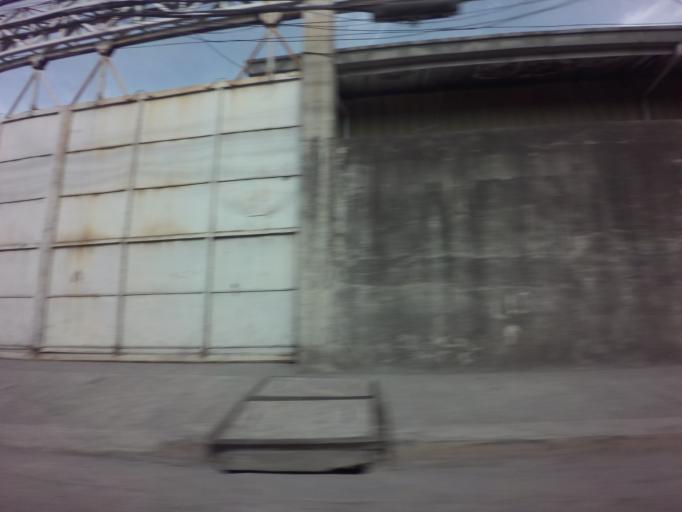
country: PH
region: Calabarzon
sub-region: Province of Rizal
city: Pateros
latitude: 14.5465
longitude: 121.0878
